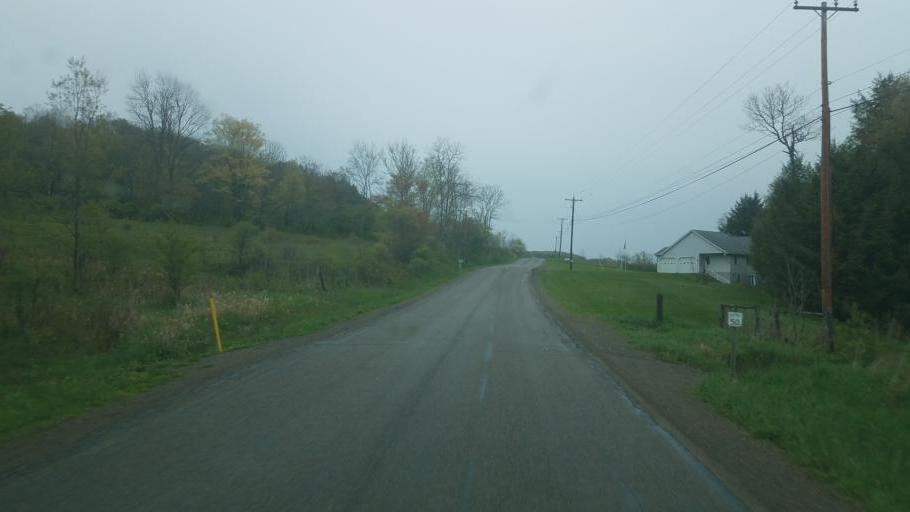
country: US
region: New York
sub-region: Allegany County
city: Andover
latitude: 41.9250
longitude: -77.7885
